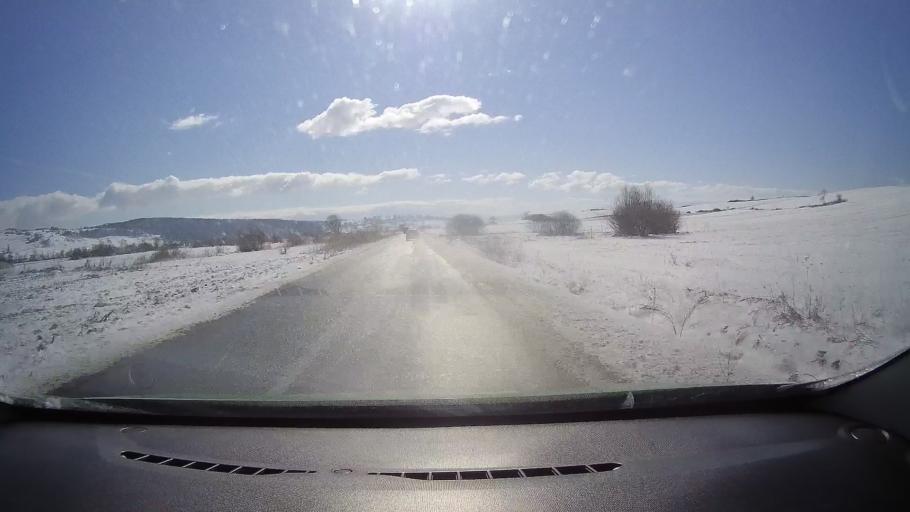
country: RO
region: Sibiu
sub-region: Comuna Vurpar
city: Vurpar
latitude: 45.8725
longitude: 24.3179
